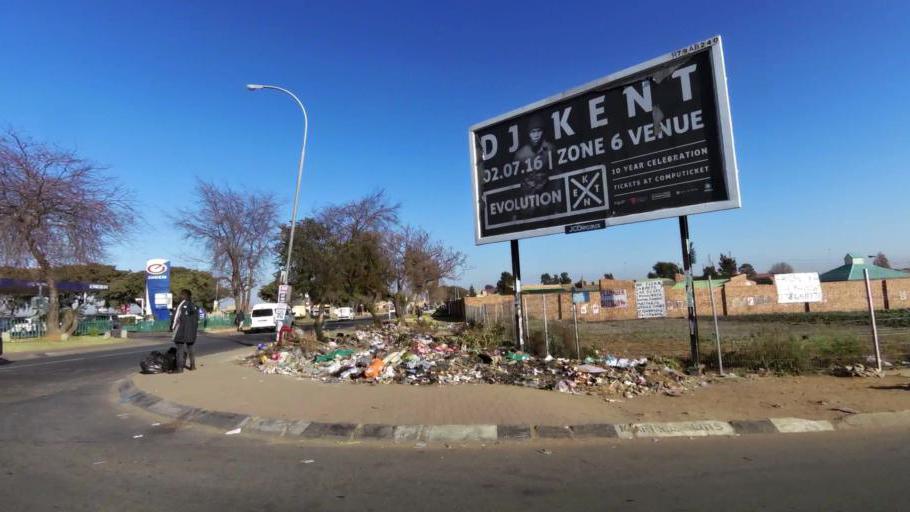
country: ZA
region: Gauteng
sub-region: City of Johannesburg Metropolitan Municipality
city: Soweto
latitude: -26.2431
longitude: 27.9408
